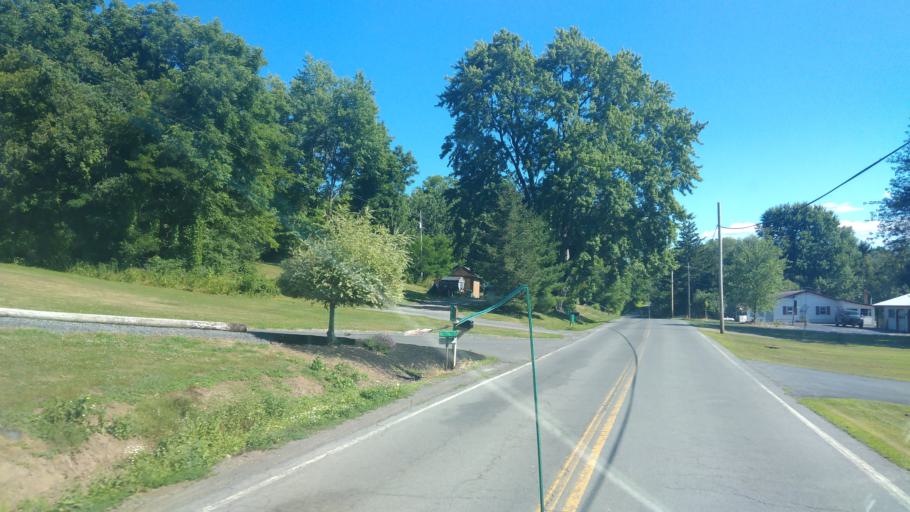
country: US
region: New York
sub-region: Wayne County
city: Clyde
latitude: 43.0112
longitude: -76.8108
